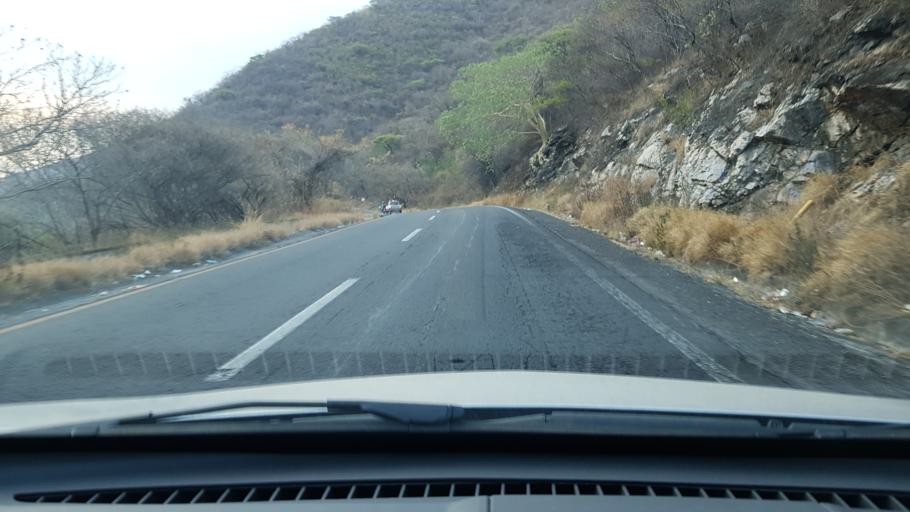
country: MX
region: Morelos
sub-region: Jiutepec
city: Independencia
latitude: 18.8592
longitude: -99.1176
